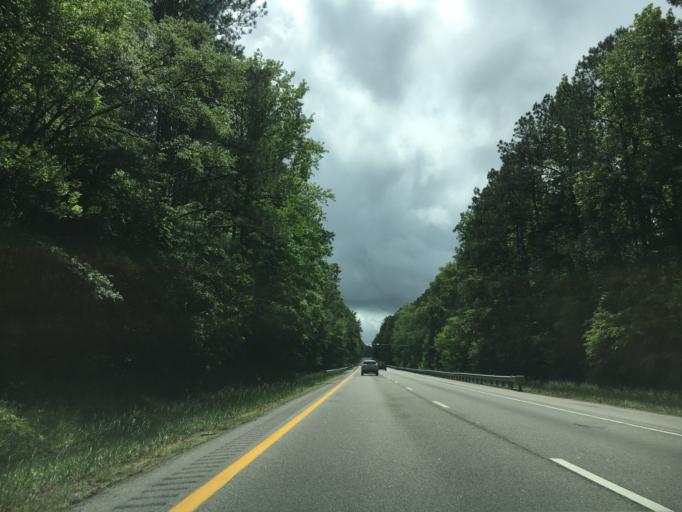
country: US
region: Virginia
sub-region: Brunswick County
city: Lawrenceville
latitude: 36.8108
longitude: -77.9763
